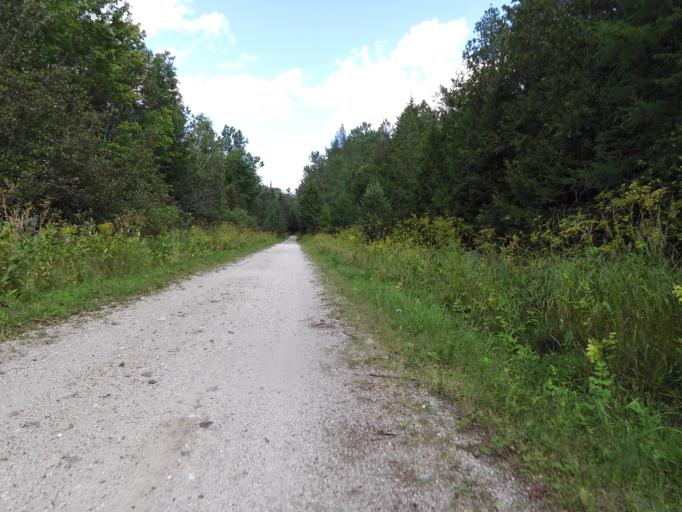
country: CA
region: Quebec
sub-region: Outaouais
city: Maniwaki
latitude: 46.0827
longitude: -76.0709
